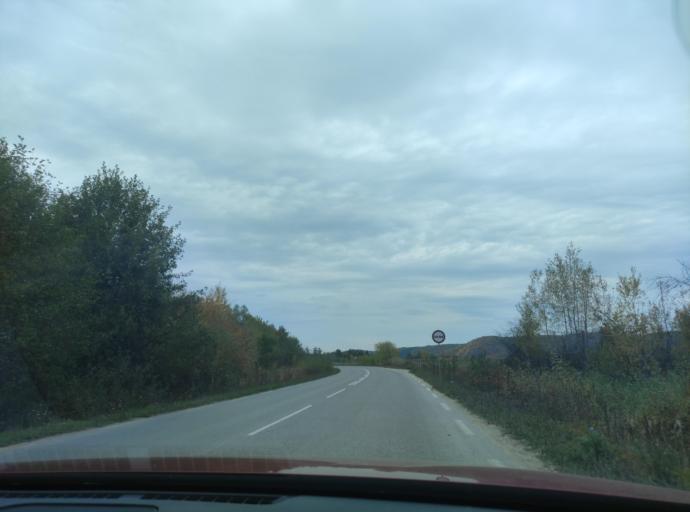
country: BG
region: Montana
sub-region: Obshtina Berkovitsa
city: Berkovitsa
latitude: 43.2386
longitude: 23.1621
